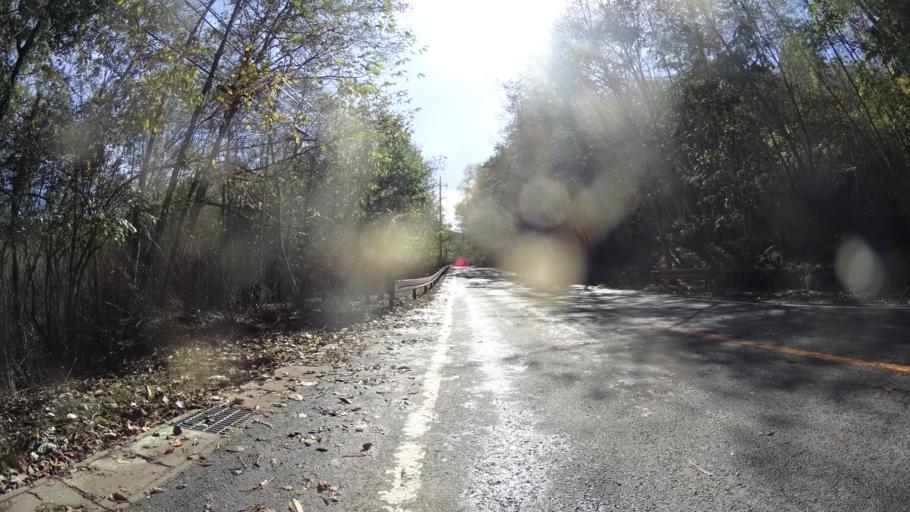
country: JP
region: Yamanashi
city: Enzan
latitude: 35.7868
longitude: 138.7995
